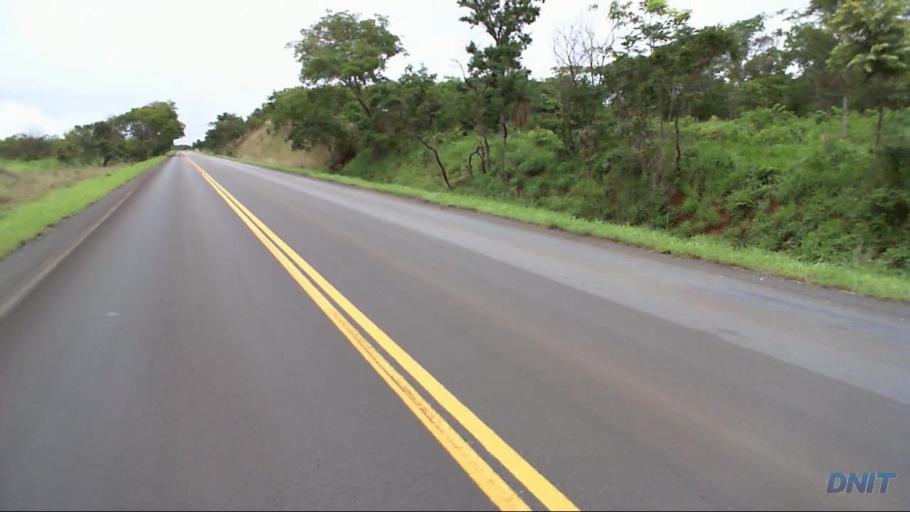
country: BR
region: Goias
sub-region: Padre Bernardo
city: Padre Bernardo
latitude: -15.1894
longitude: -48.4352
